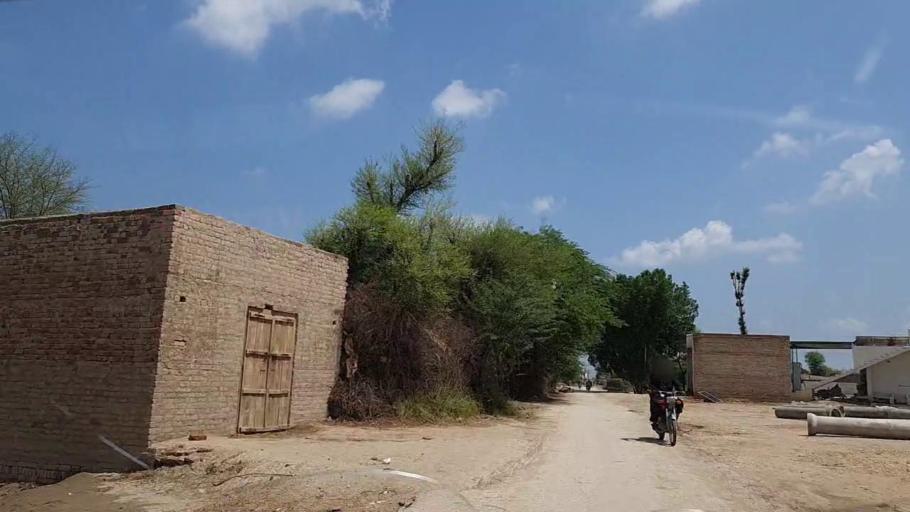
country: PK
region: Sindh
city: Tharu Shah
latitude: 26.9922
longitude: 68.0729
